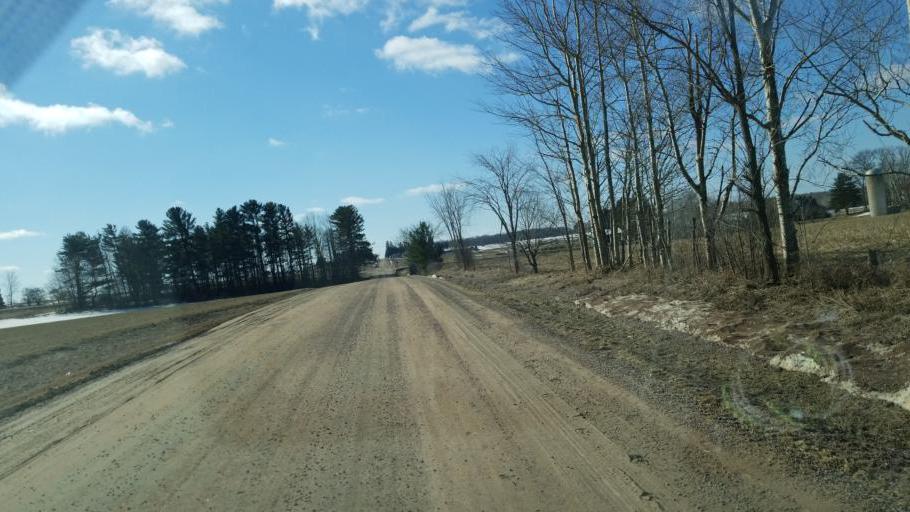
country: US
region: Wisconsin
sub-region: Clark County
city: Loyal
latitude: 44.6571
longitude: -90.4562
